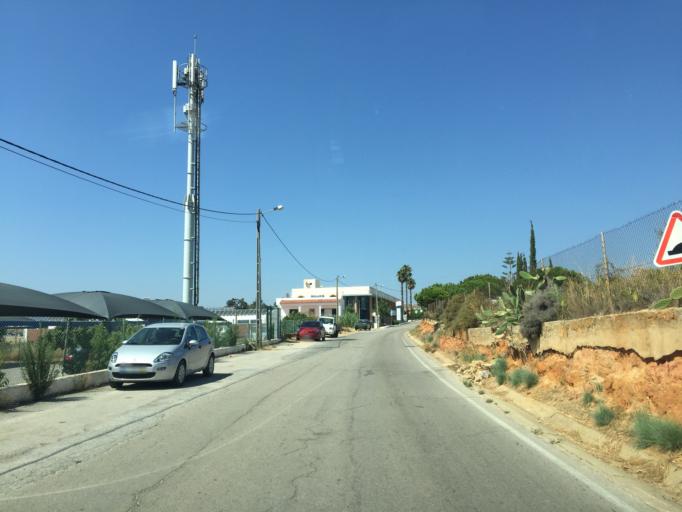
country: PT
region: Faro
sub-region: Faro
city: Faro
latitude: 37.0391
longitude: -7.8963
